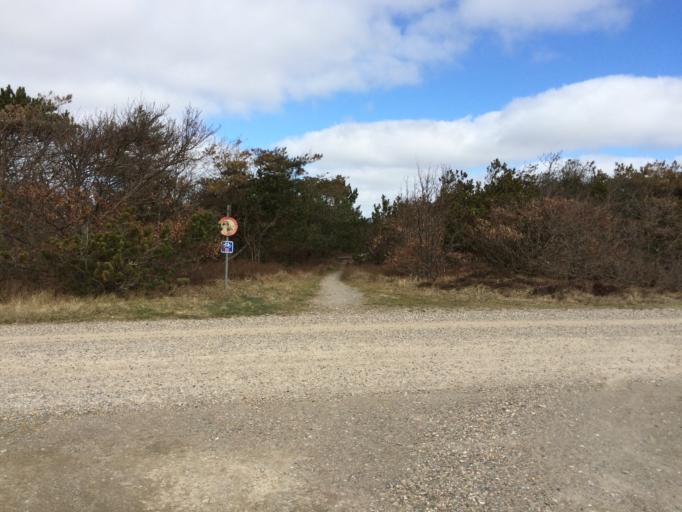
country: DK
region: Central Jutland
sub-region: Holstebro Kommune
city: Ulfborg
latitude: 56.3162
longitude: 8.1323
